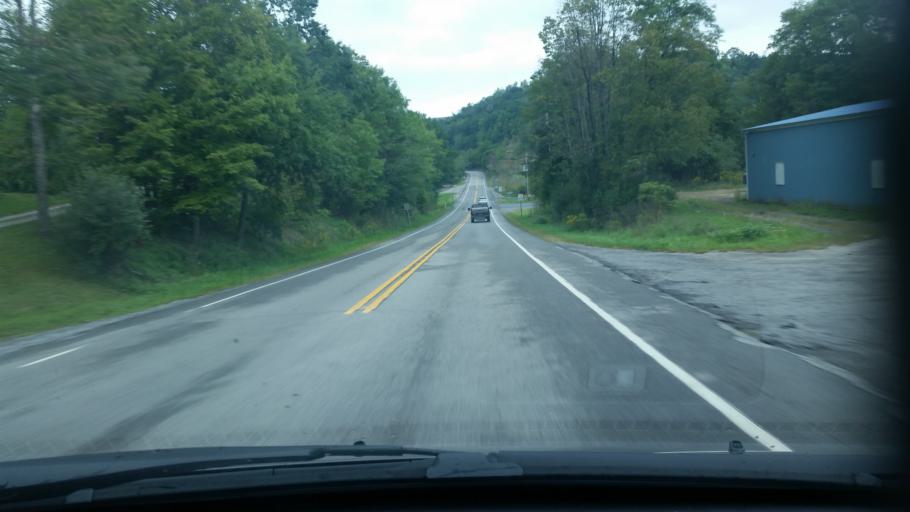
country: US
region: Pennsylvania
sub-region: Clearfield County
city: Shiloh
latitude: 41.0721
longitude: -78.3254
